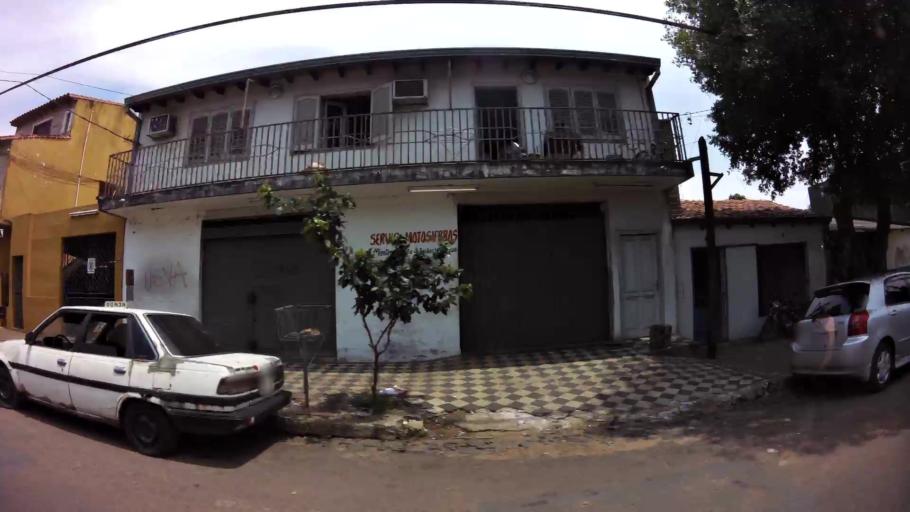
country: PY
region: Central
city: Fernando de la Mora
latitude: -25.3162
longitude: -57.5609
